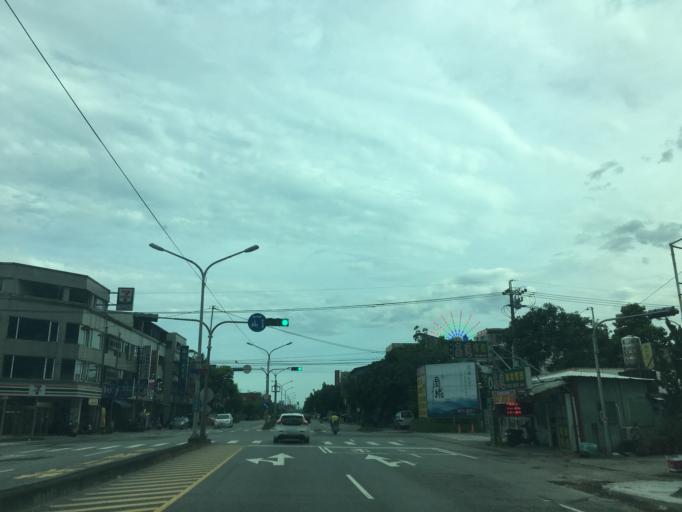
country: TW
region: Taiwan
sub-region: Hualien
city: Hualian
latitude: 24.0372
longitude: 121.6046
